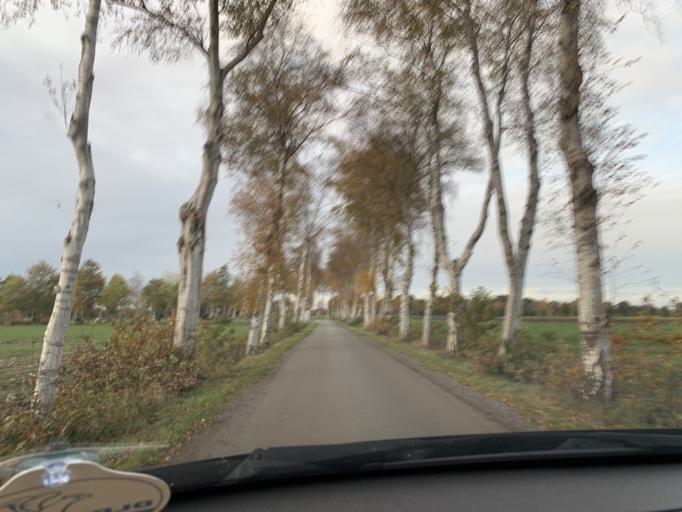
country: DE
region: Lower Saxony
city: Wiefelstede
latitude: 53.2632
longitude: 8.0673
